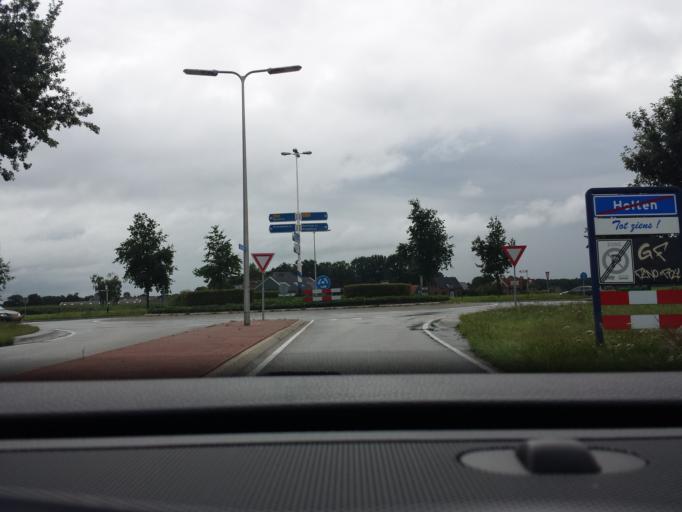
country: NL
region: Overijssel
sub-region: Gemeente Hof van Twente
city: Markelo
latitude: 52.2844
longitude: 6.4368
